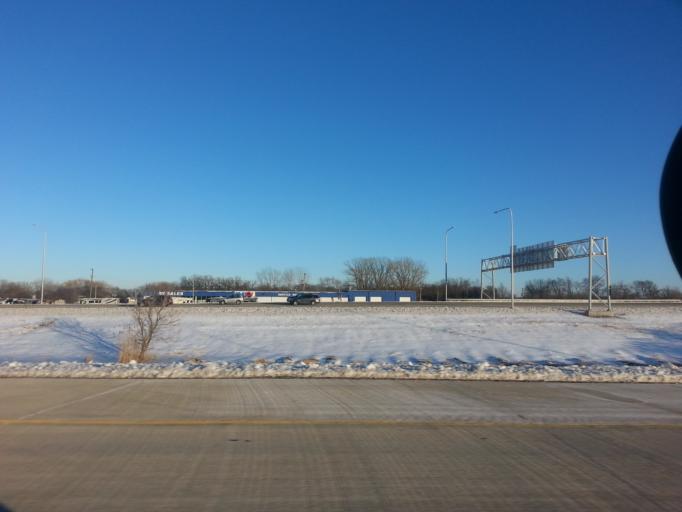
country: US
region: Illinois
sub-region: Lake County
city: Wadsworth
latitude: 42.4837
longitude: -87.9474
